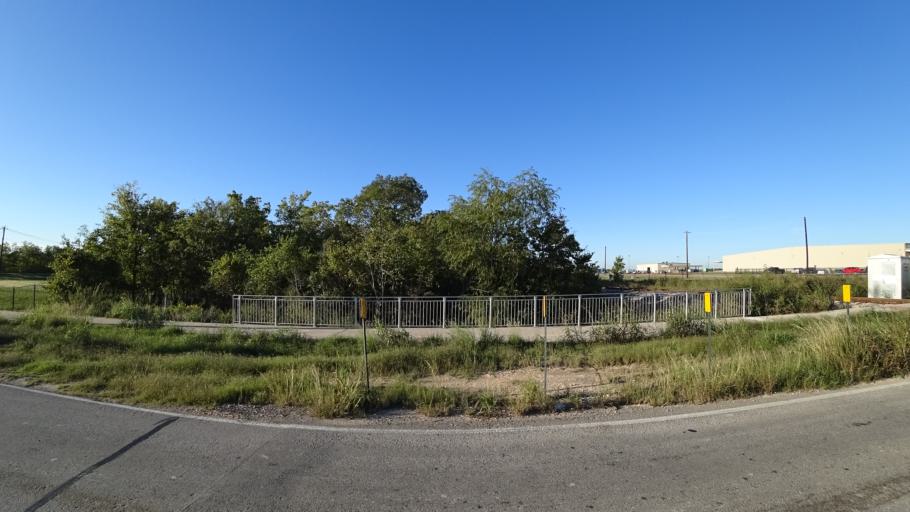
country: US
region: Texas
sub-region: Travis County
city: Manor
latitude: 30.3200
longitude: -97.6266
